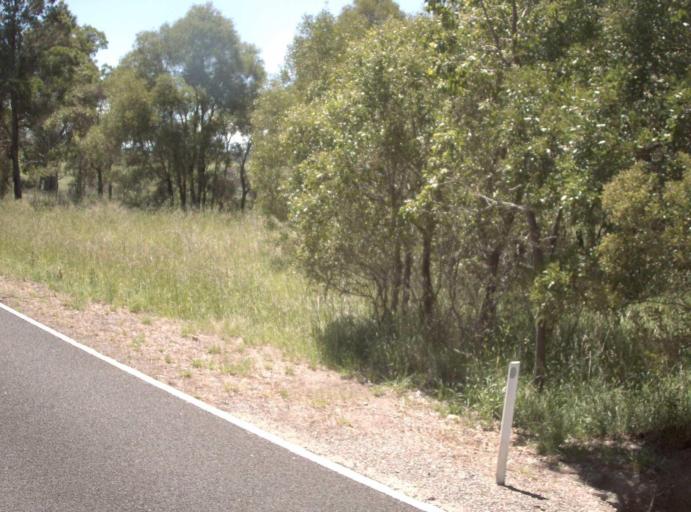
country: AU
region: Victoria
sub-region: East Gippsland
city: Lakes Entrance
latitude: -37.2502
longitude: 148.2509
